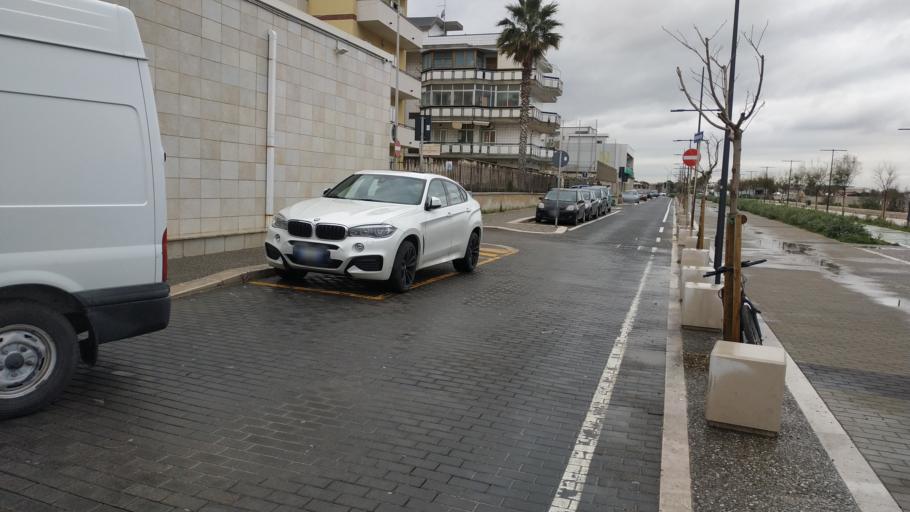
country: IT
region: Apulia
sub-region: Provincia di Bari
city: San Paolo
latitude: 41.1397
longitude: 16.8131
